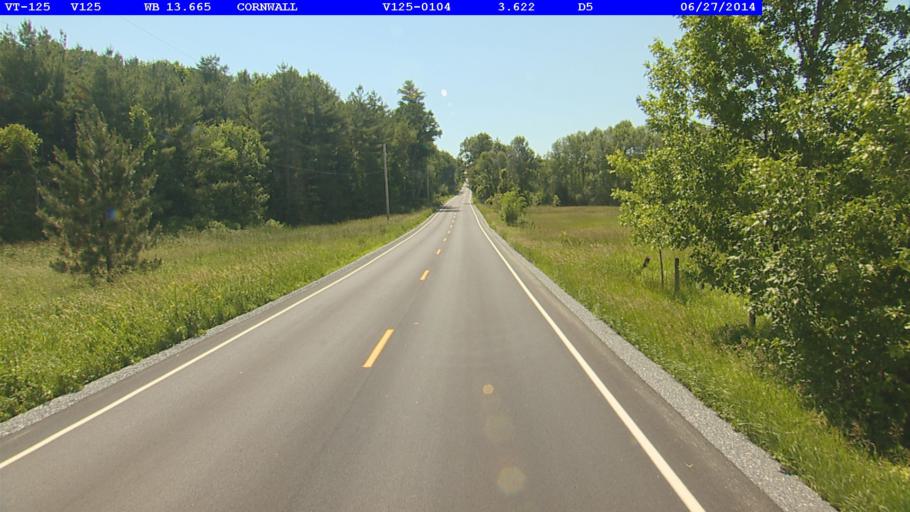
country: US
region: Vermont
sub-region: Addison County
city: Middlebury (village)
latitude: 44.0081
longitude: -73.2015
